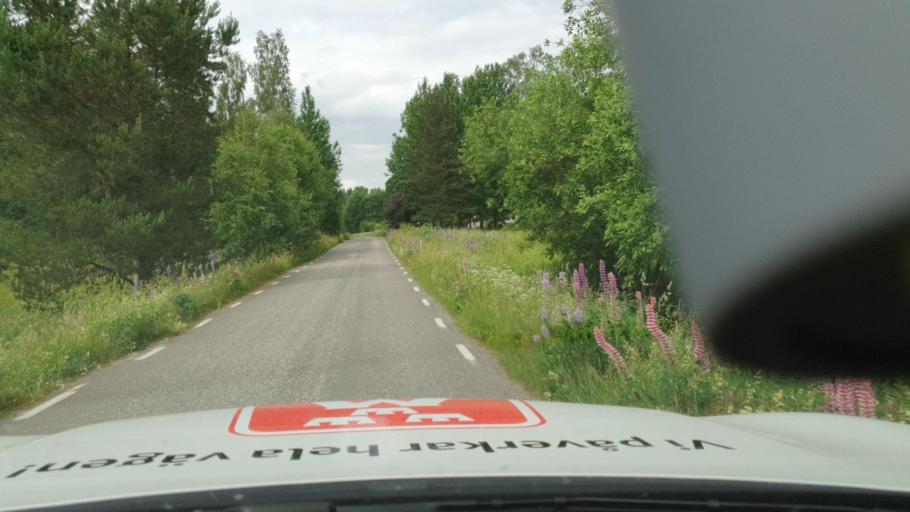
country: SE
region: Vaestra Goetaland
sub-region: Tidaholms Kommun
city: Tidaholm
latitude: 58.1692
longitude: 14.0146
